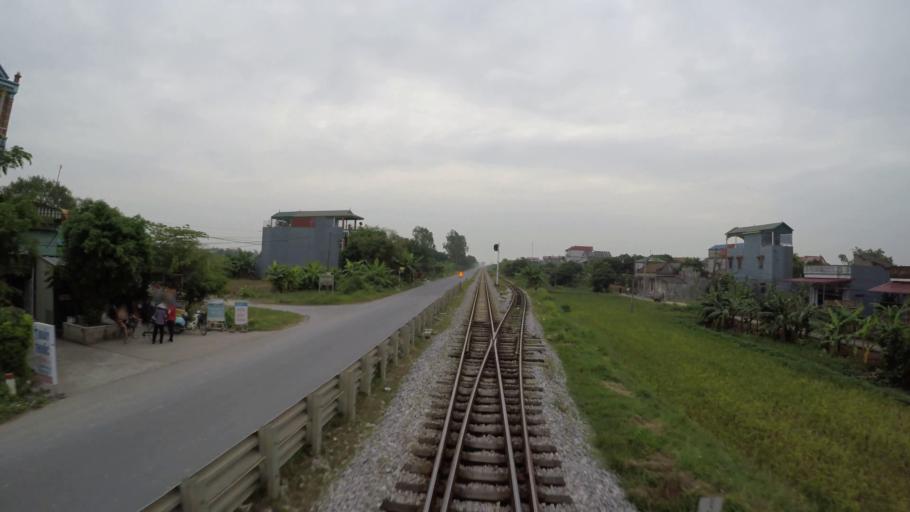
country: VN
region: Hung Yen
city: Ban Yen Nhan
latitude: 20.9736
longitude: 106.0944
